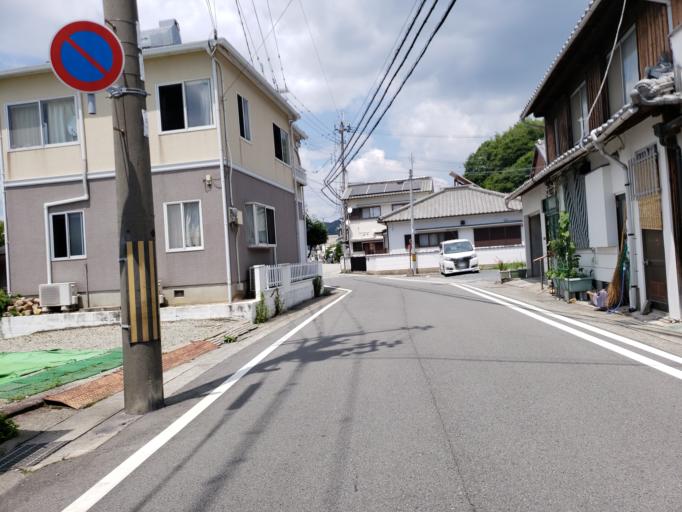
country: JP
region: Hyogo
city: Kariya
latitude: 34.7320
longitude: 134.4076
